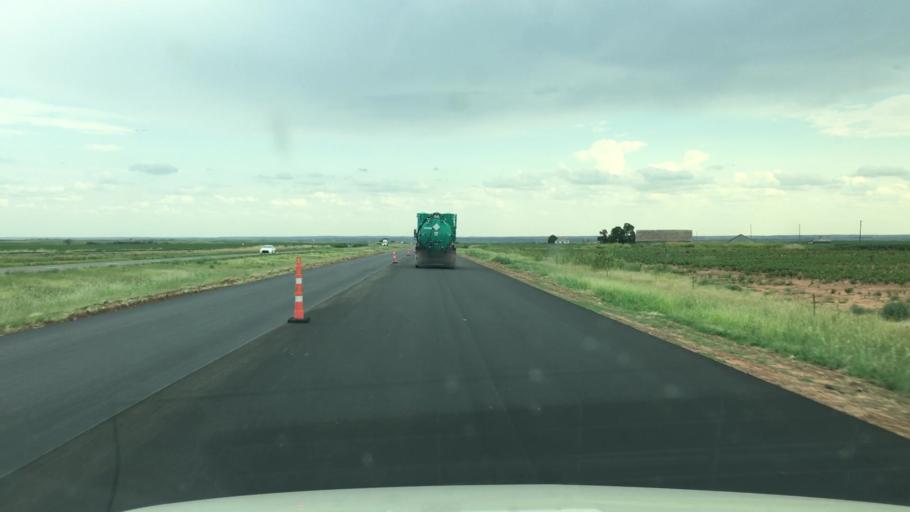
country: US
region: Texas
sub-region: Hall County
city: Memphis
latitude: 34.6218
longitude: -100.4728
